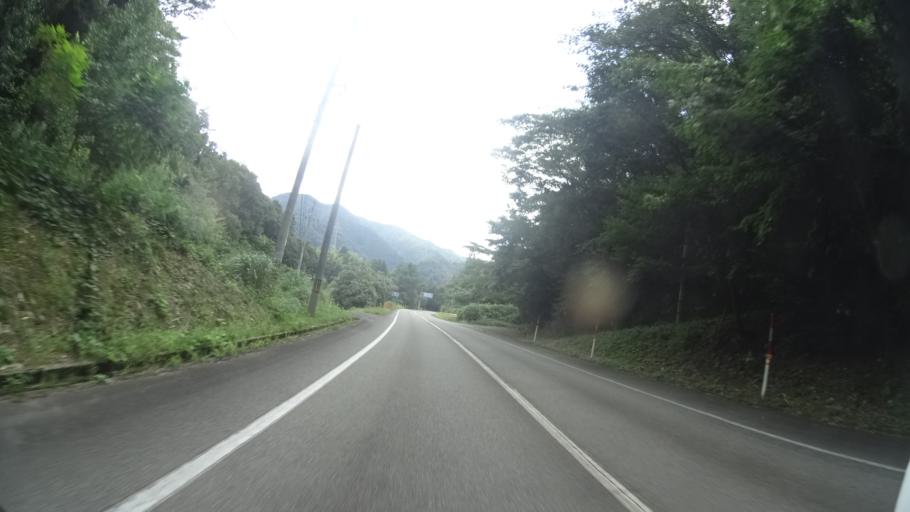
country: JP
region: Yamaguchi
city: Hagi
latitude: 34.5537
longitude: 131.6047
